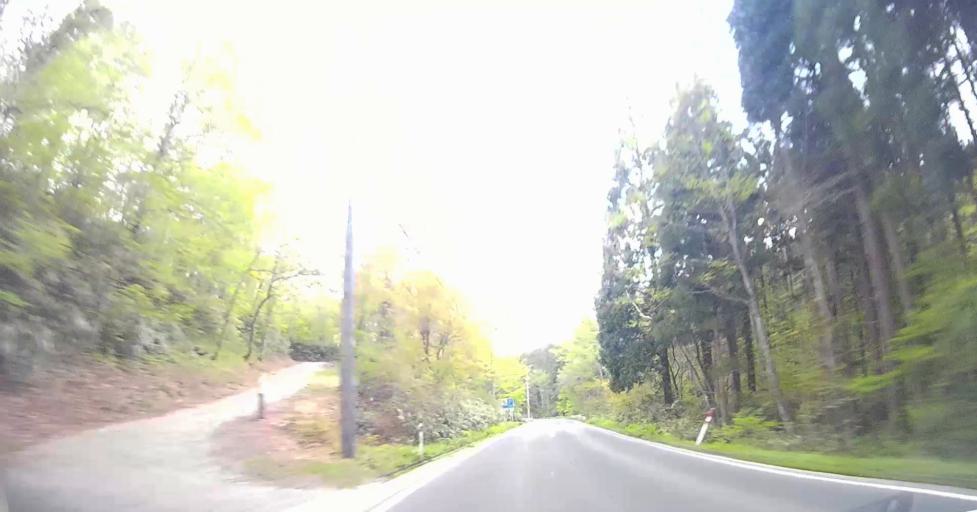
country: JP
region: Aomori
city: Goshogawara
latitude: 41.0918
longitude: 140.5537
